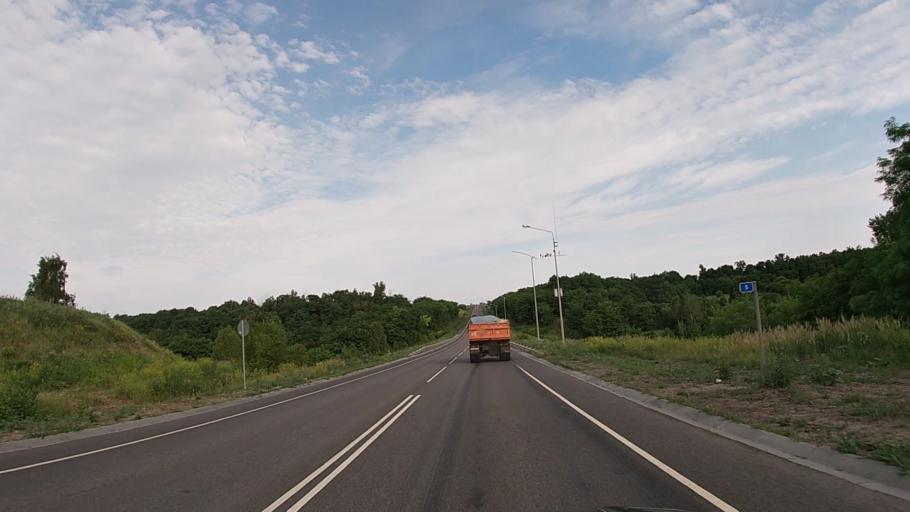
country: RU
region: Belgorod
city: Severnyy
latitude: 50.6678
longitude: 36.4917
